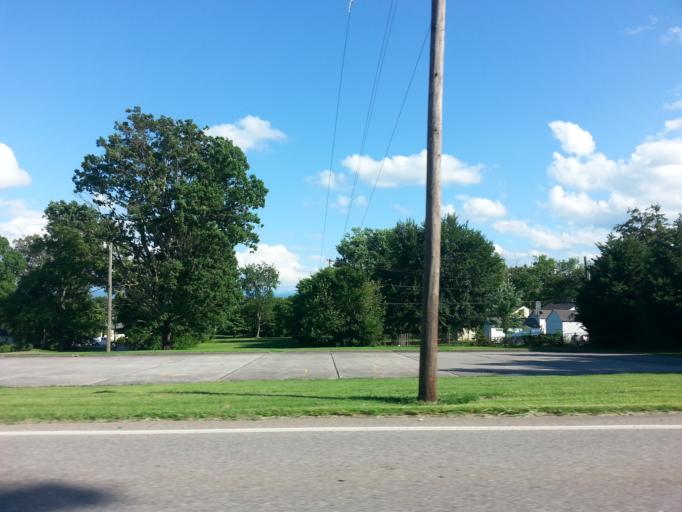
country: US
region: Tennessee
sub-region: Blount County
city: Alcoa
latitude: 35.8046
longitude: -83.9782
